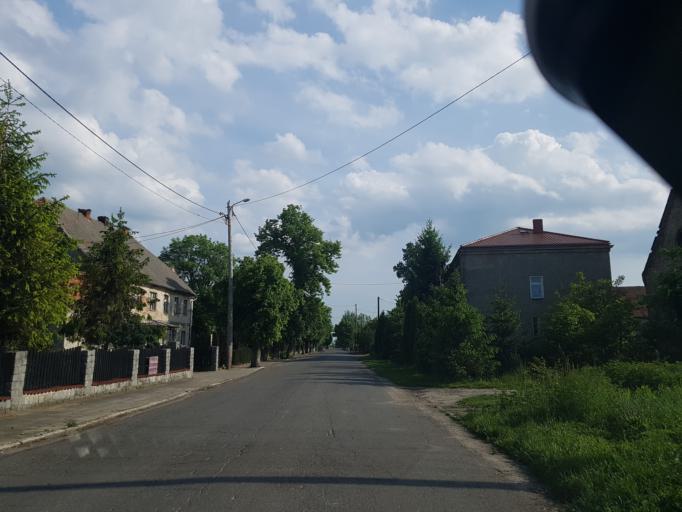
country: PL
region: Lower Silesian Voivodeship
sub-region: Powiat strzelinski
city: Wiazow
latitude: 50.8689
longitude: 17.1564
